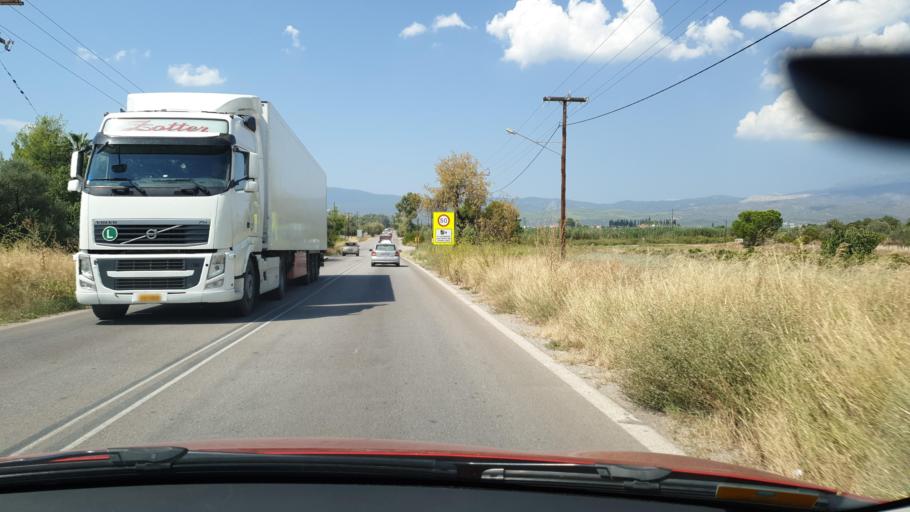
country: GR
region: Central Greece
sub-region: Nomos Evvoias
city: Nea Artaki
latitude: 38.5365
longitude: 23.6316
